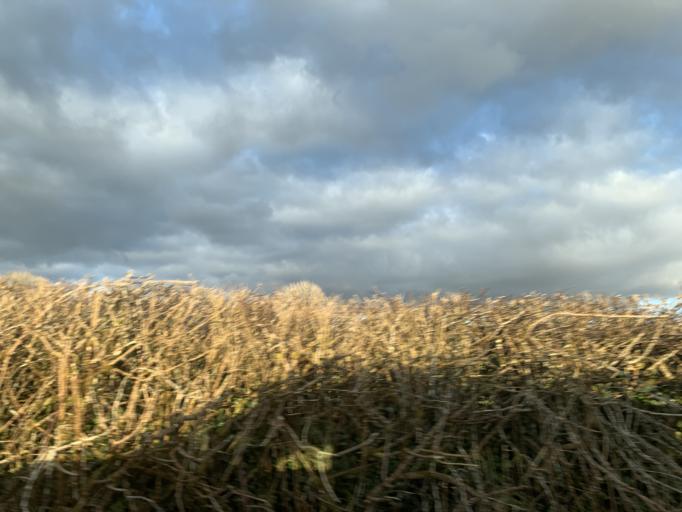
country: IE
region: Connaught
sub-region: Maigh Eo
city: Ballyhaunis
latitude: 53.8224
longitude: -8.6999
